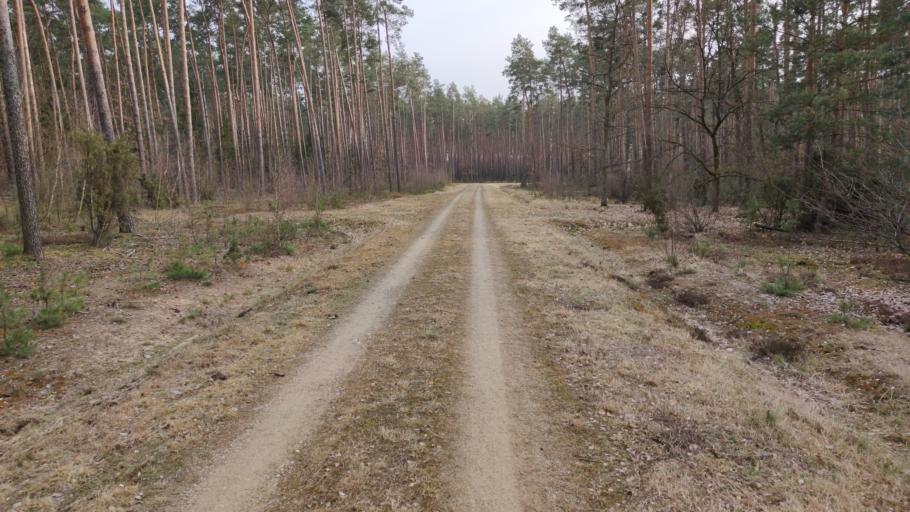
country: PL
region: Masovian Voivodeship
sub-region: Powiat plocki
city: Bodzanow
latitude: 52.4497
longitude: 19.9629
